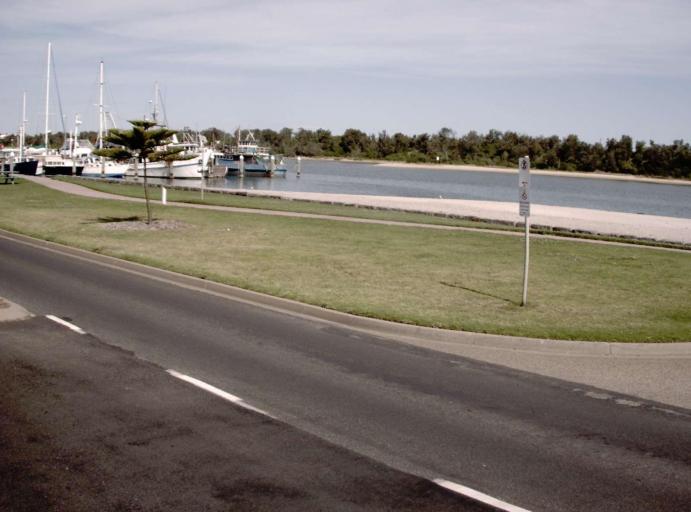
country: AU
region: Victoria
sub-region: East Gippsland
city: Lakes Entrance
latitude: -37.8812
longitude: 147.9859
